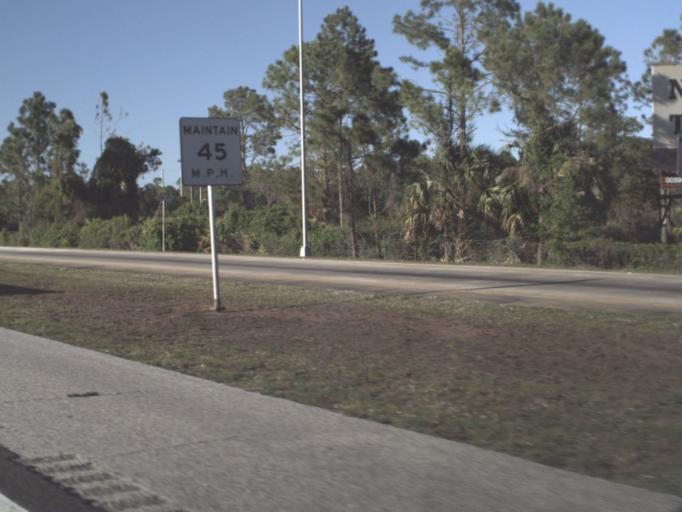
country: US
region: Florida
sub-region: Flagler County
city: Flagler Beach
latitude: 29.5049
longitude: -81.1946
